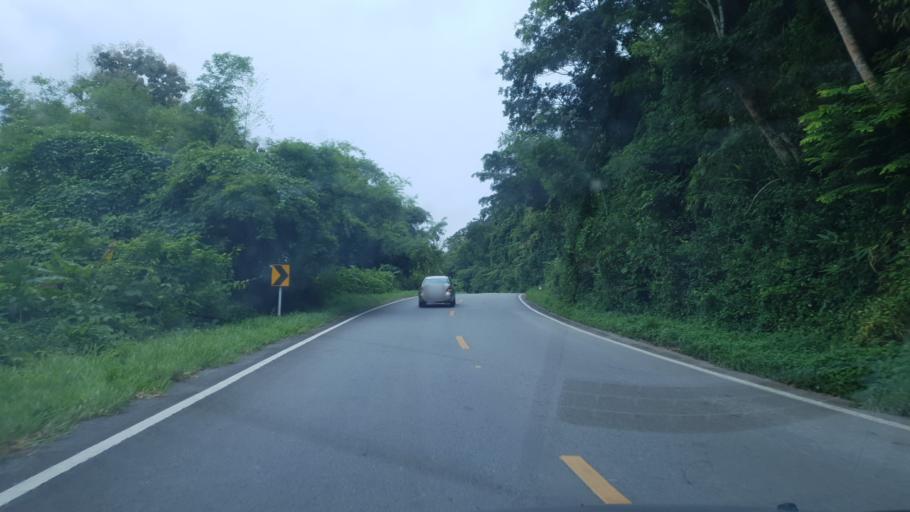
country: TH
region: Mae Hong Son
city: Khun Yuam
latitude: 18.7192
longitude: 97.9082
